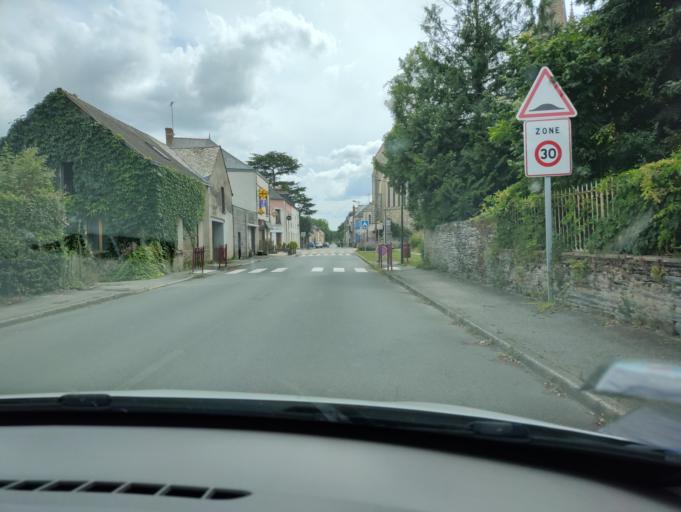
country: FR
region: Pays de la Loire
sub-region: Departement de la Loire-Atlantique
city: Saint-Vincent-des-Landes
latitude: 47.6202
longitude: -1.5373
